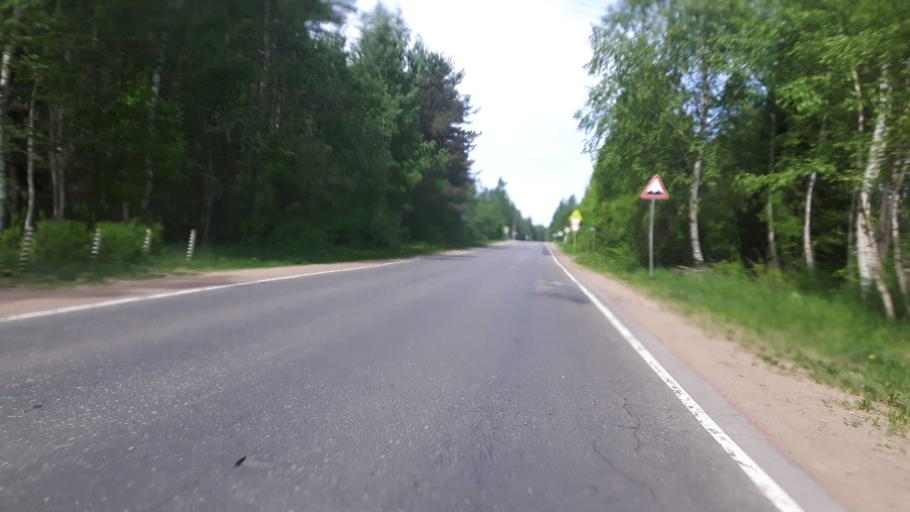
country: RU
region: Leningrad
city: Ust'-Luga
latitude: 59.6442
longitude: 28.2709
